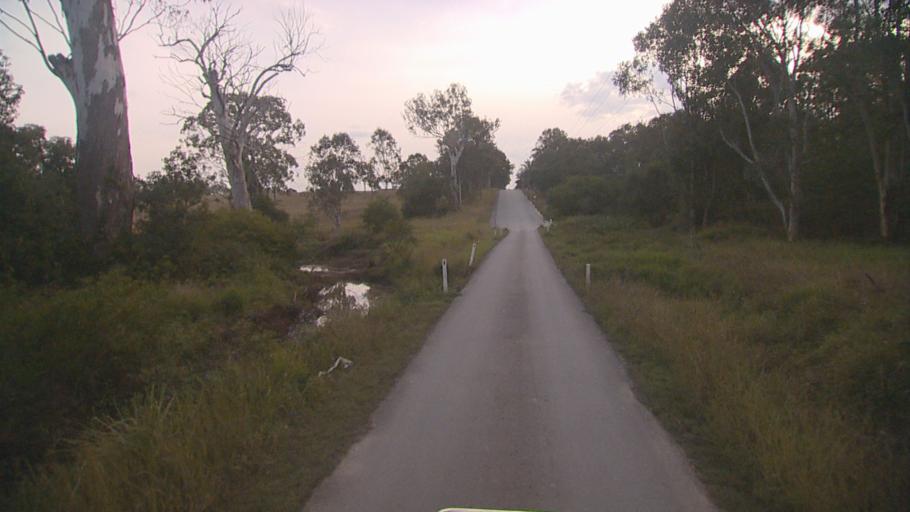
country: AU
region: Queensland
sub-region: Logan
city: Cedar Vale
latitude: -27.8570
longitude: 153.1190
